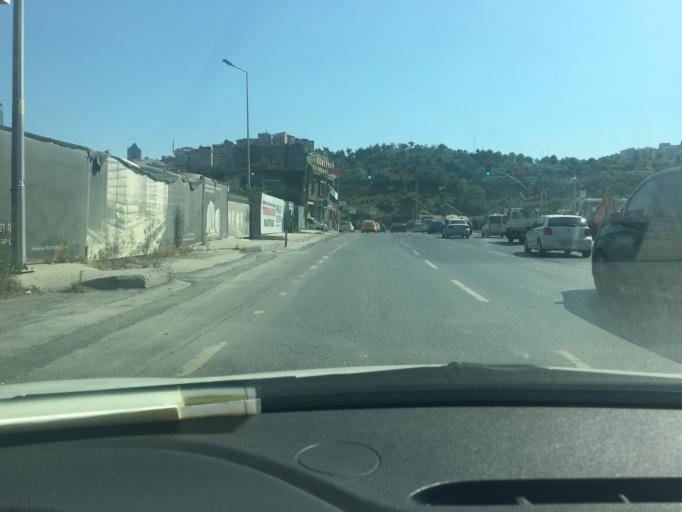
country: TR
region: Istanbul
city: Sisli
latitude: 41.0885
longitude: 28.9830
